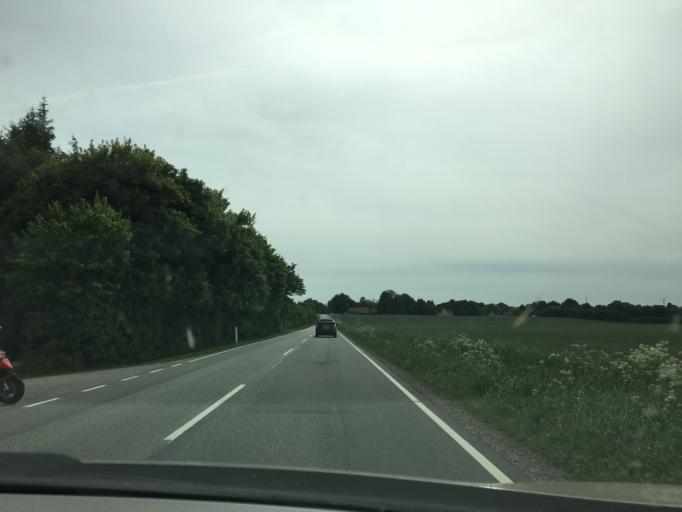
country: DK
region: Central Jutland
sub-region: Norddjurs Kommune
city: Allingabro
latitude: 56.4503
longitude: 10.2893
